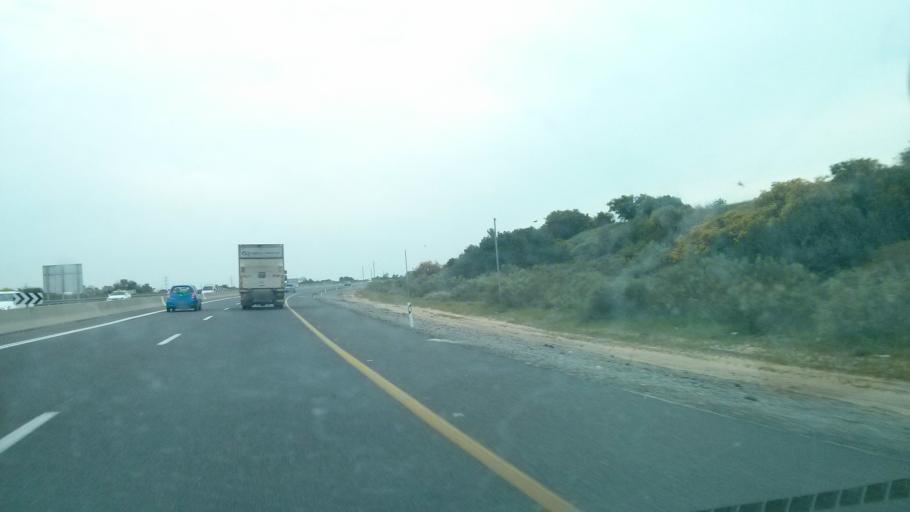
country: IL
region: Haifa
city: Qesarya
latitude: 32.4948
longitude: 34.9180
